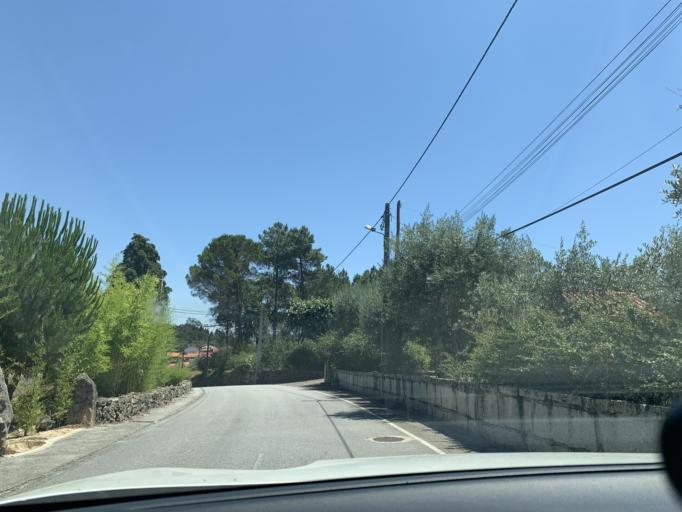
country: PT
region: Viseu
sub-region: Mangualde
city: Mangualde
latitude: 40.5608
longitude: -7.6918
